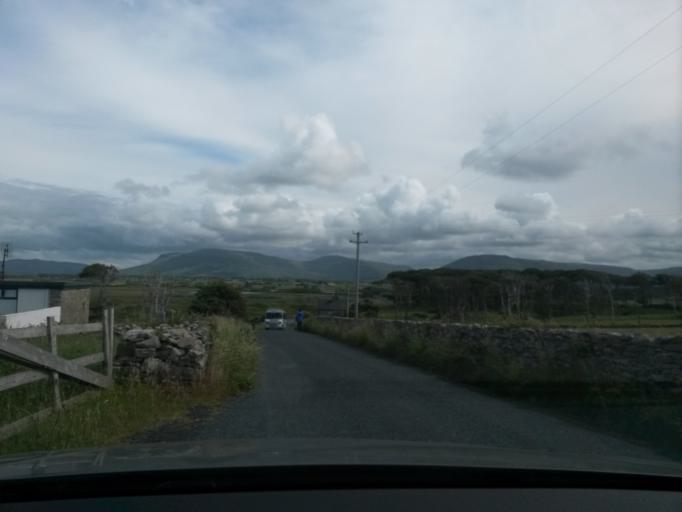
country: IE
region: Ulster
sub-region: County Donegal
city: Killybegs
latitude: 54.4590
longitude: -8.4578
